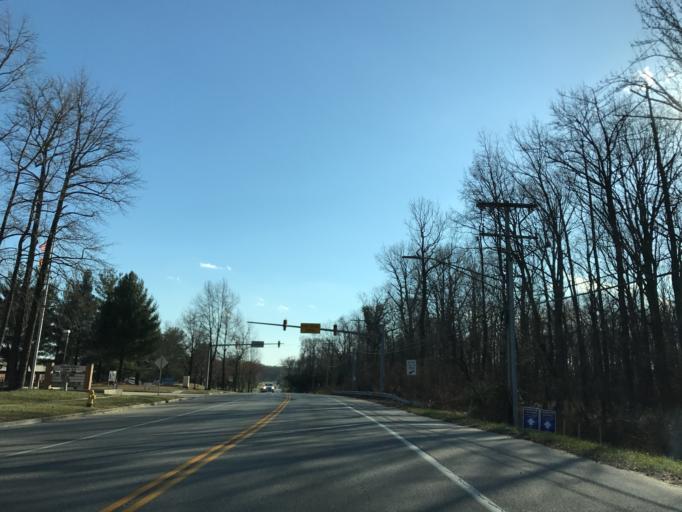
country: US
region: Maryland
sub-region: Anne Arundel County
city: Green Haven
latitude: 39.1794
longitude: -76.5504
